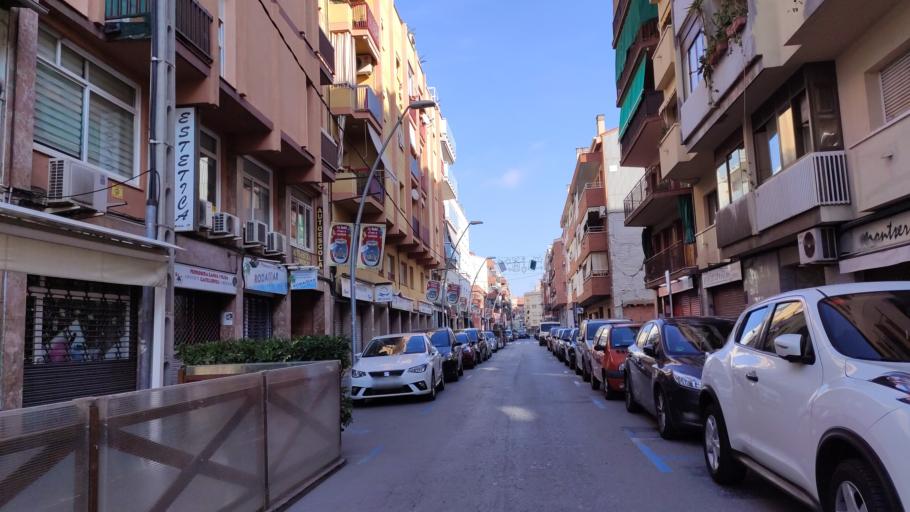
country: ES
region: Catalonia
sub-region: Provincia de Barcelona
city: Castelldefels
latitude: 41.2776
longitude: 1.9756
